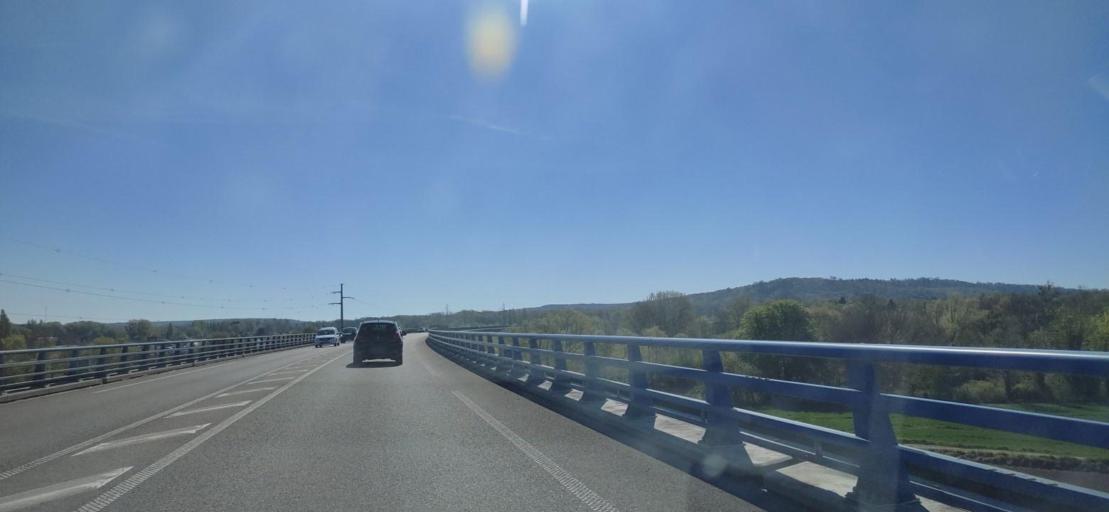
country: FR
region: Picardie
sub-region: Departement de l'Oise
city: Choisy-au-Bac
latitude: 49.4342
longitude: 2.8637
